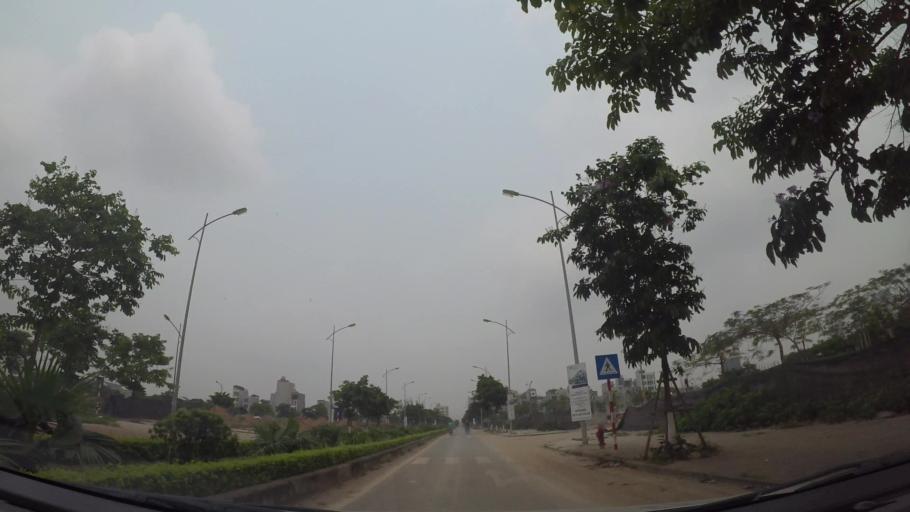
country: VN
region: Ha Noi
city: Ha Dong
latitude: 20.9839
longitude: 105.7536
